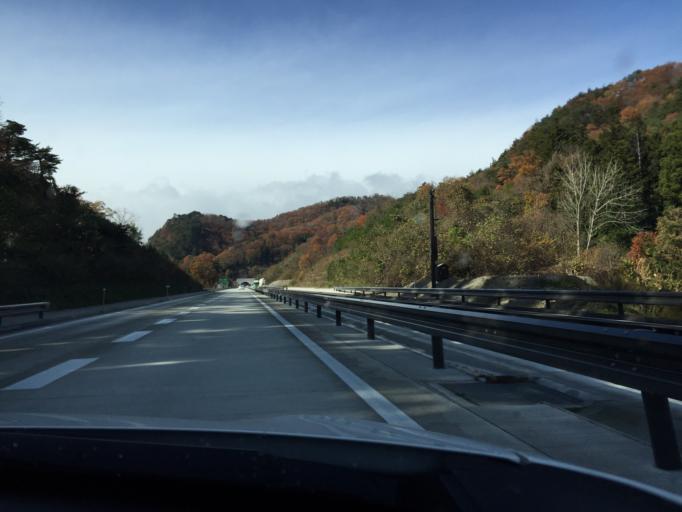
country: JP
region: Fukushima
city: Fukushima-shi
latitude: 37.8353
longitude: 140.3883
